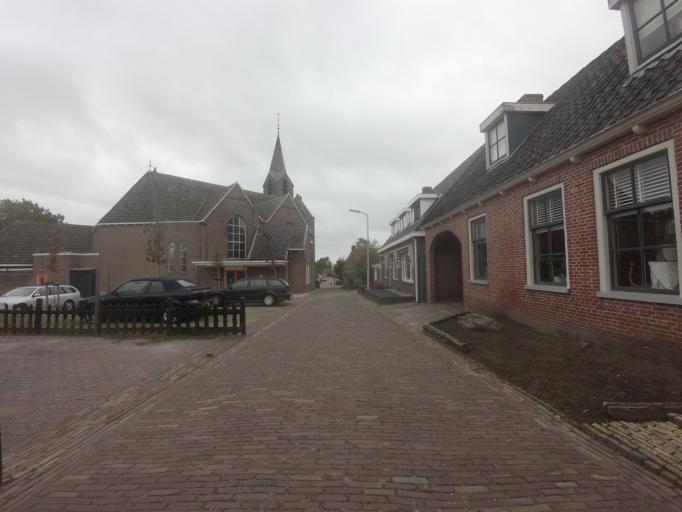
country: NL
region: Friesland
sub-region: Gemeente Ferwerderadiel
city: Hallum
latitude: 53.3064
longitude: 5.7850
